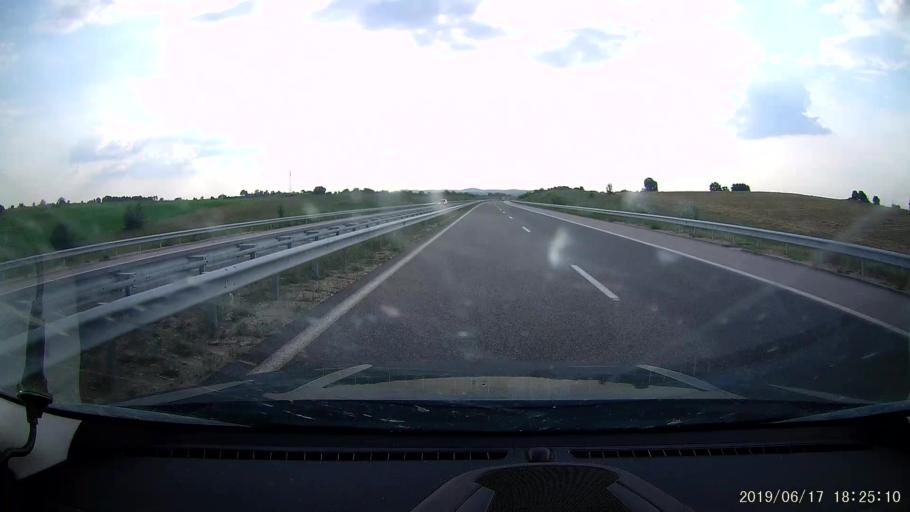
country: BG
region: Khaskovo
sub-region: Obshtina Dimitrovgrad
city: Dimitrovgrad
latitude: 41.9895
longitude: 25.6693
